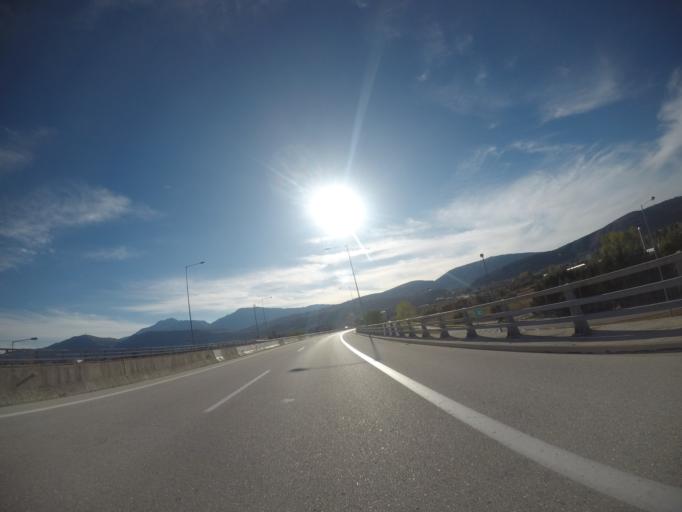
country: GR
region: Epirus
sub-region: Nomos Ioanninon
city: Pedini
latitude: 39.5962
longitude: 20.8625
